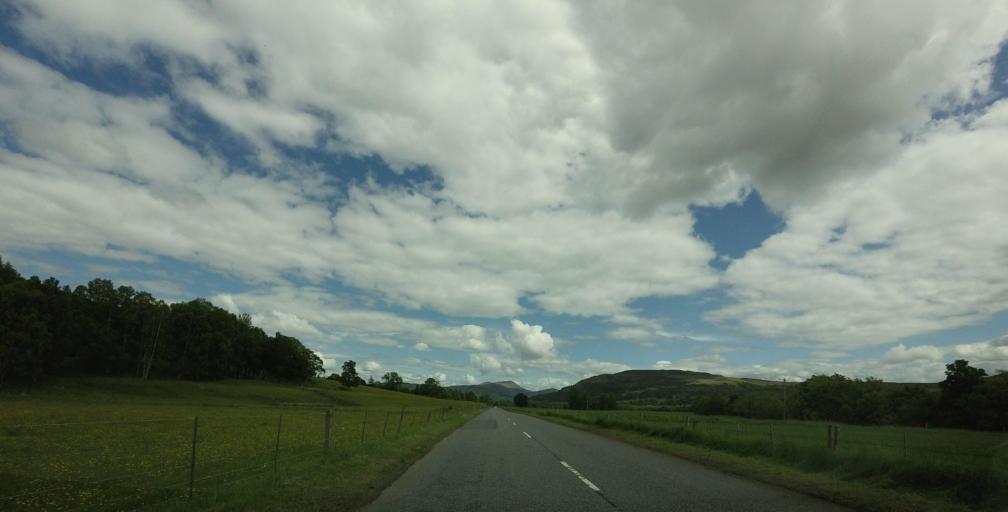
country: GB
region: Scotland
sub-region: Perth and Kinross
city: Aberfeldy
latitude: 56.7707
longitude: -3.9183
